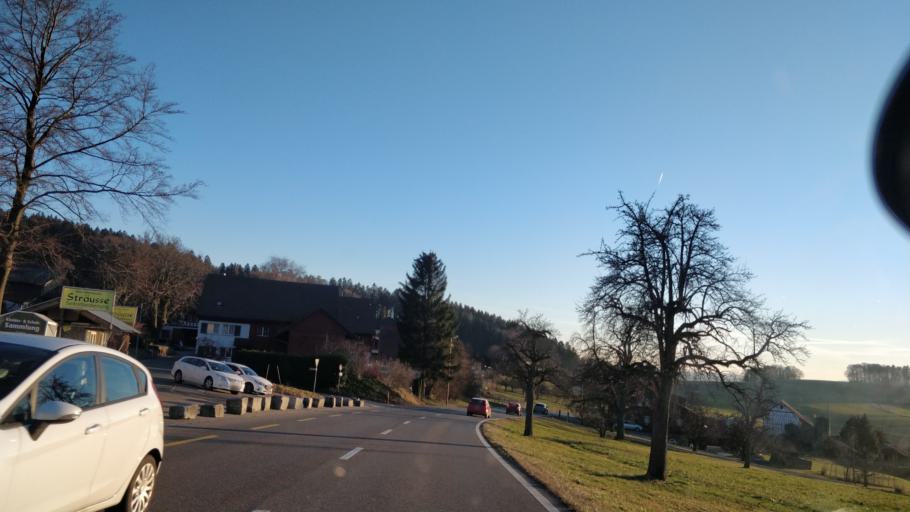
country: CH
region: Zurich
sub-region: Bezirk Buelach
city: Rorbas
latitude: 47.5182
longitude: 8.5663
